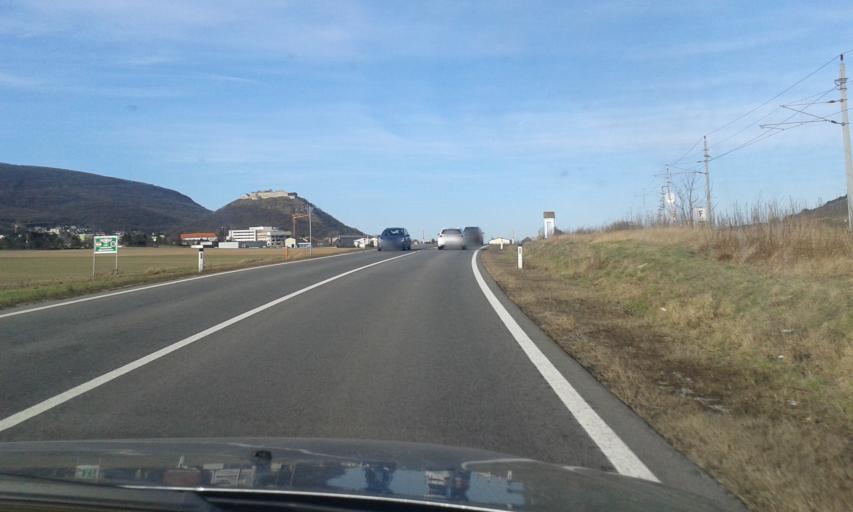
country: AT
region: Lower Austria
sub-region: Politischer Bezirk Bruck an der Leitha
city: Hainburg an der Donau
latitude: 48.1442
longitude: 16.9723
